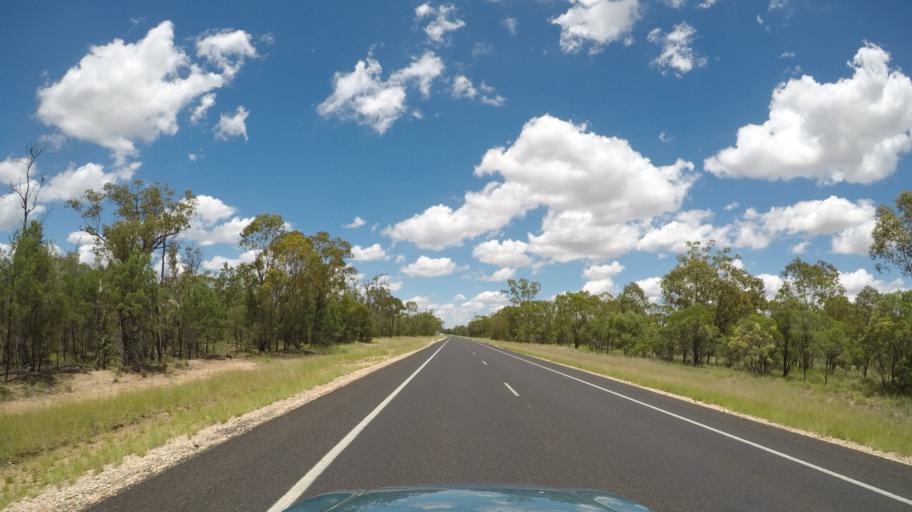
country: AU
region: Queensland
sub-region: Goondiwindi
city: Goondiwindi
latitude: -28.0702
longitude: 150.7522
